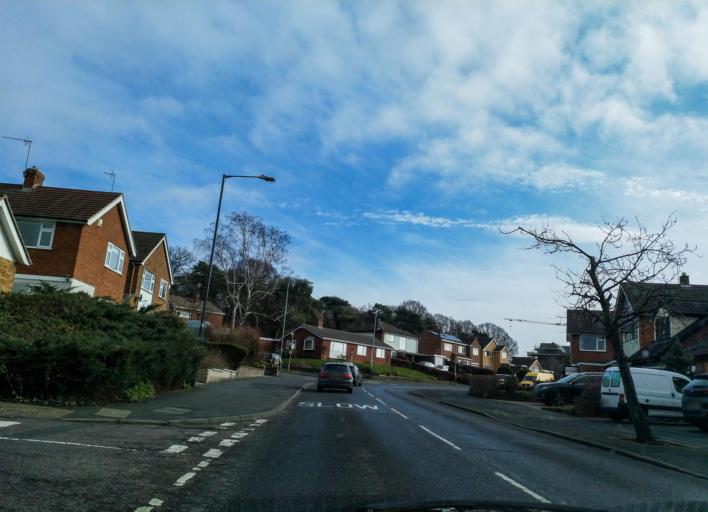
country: GB
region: England
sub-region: Warwickshire
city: Warwick
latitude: 52.2936
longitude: -1.5742
